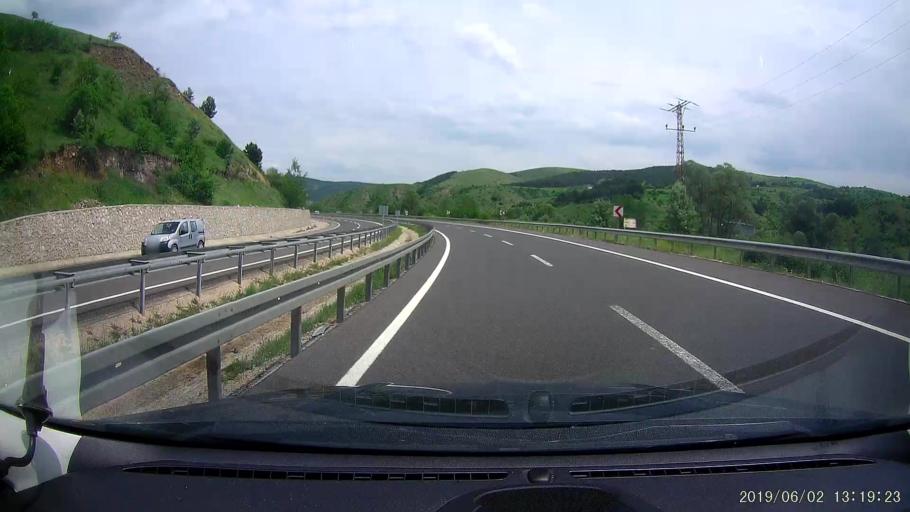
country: TR
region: Cankiri
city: Cerkes
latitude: 40.8327
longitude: 32.7343
